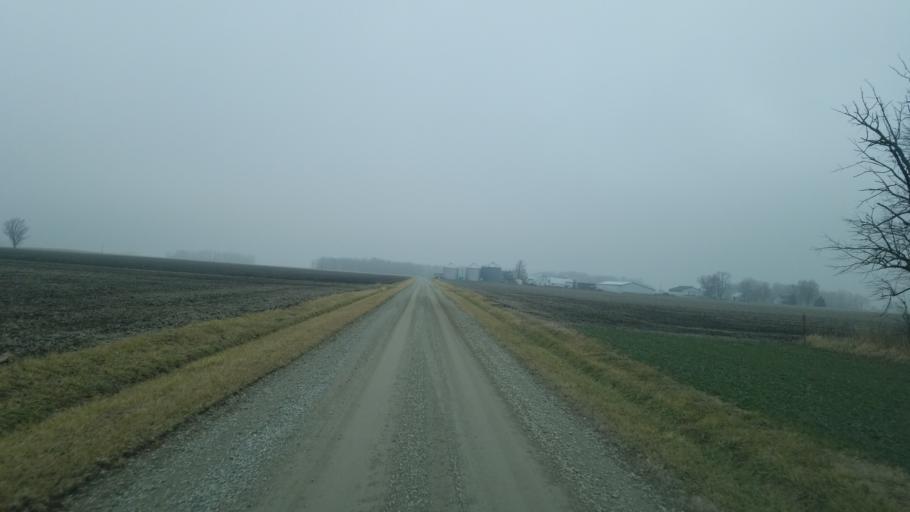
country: US
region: Indiana
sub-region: Adams County
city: Berne
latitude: 40.6360
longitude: -85.0700
